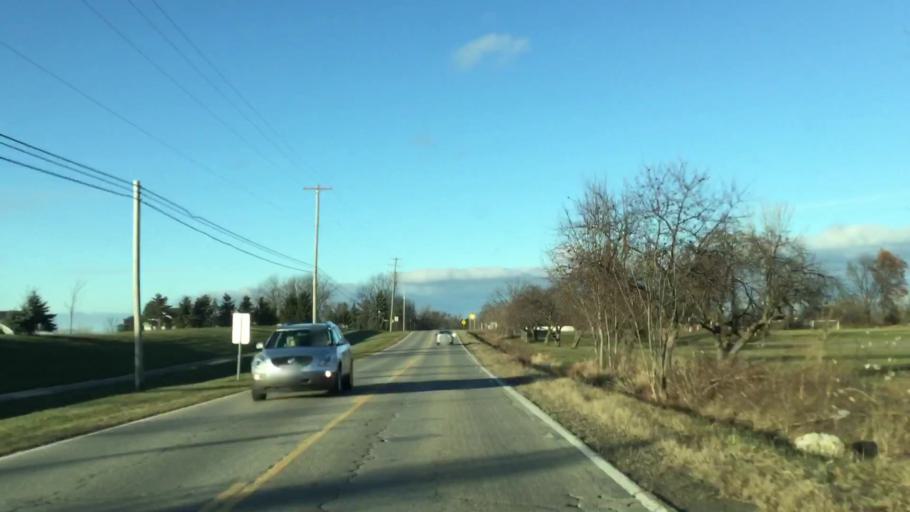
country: US
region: Michigan
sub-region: Genesee County
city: Linden
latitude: 42.7941
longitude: -83.7864
